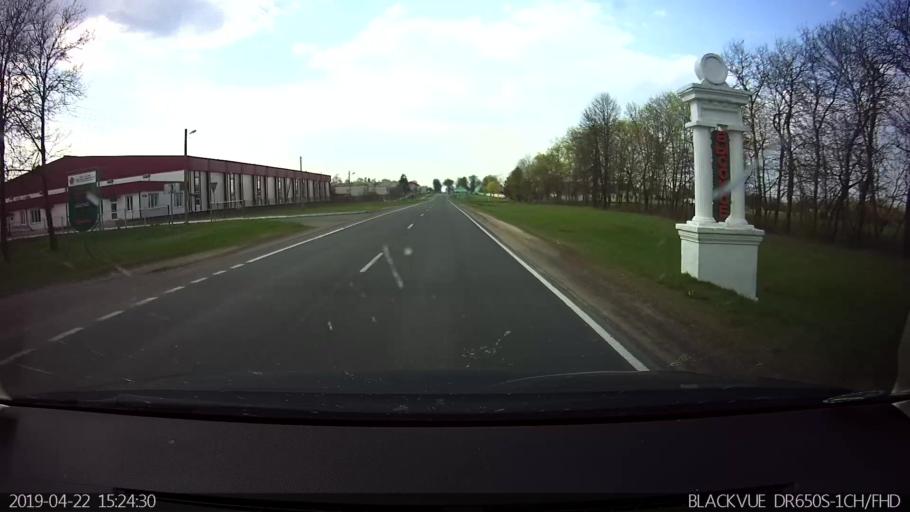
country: BY
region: Brest
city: Vysokaye
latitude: 52.3611
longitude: 23.4071
